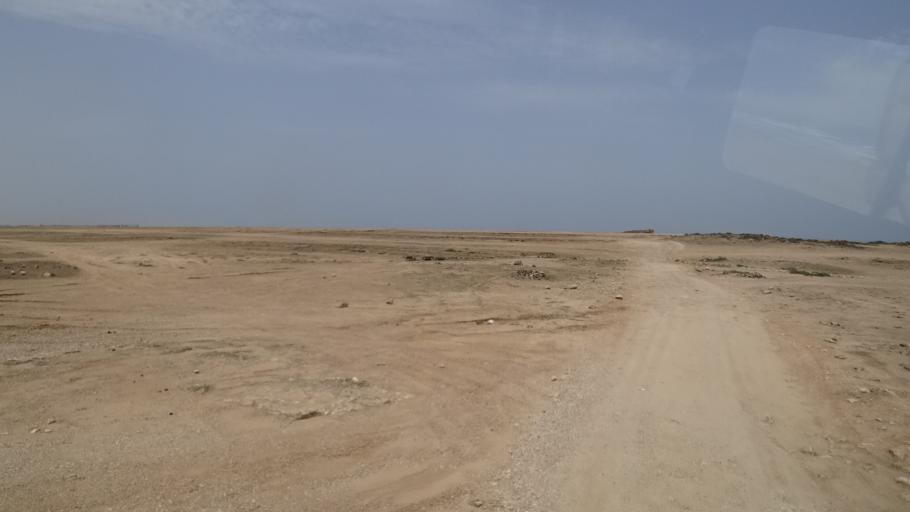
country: OM
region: Zufar
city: Salalah
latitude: 17.0345
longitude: 54.4096
